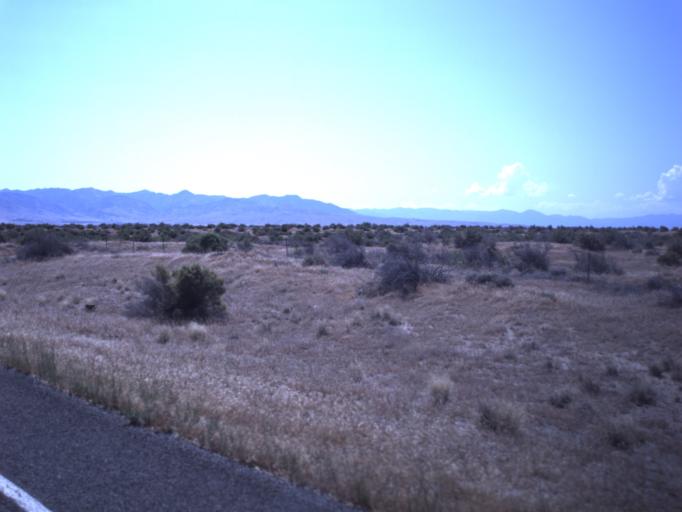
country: US
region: Utah
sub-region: Millard County
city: Delta
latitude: 39.4768
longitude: -112.4920
